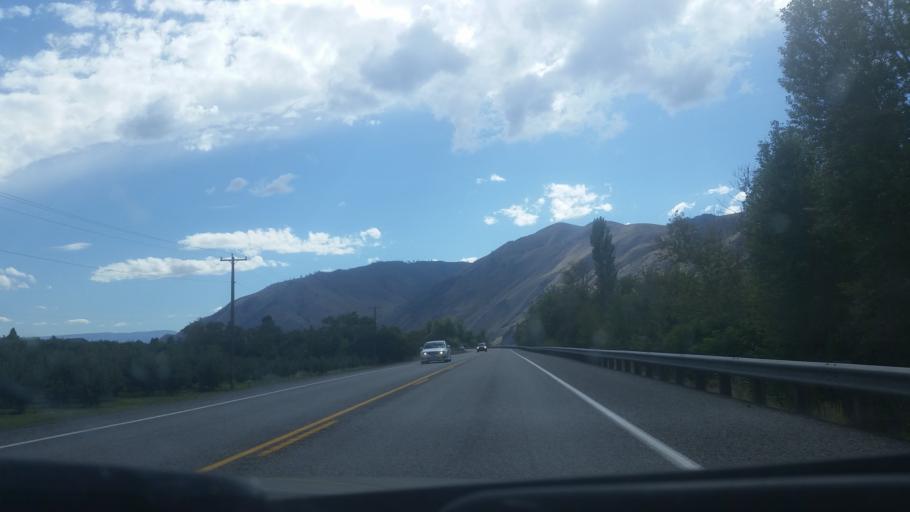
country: US
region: Washington
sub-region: Chelan County
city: Entiat
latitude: 47.6615
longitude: -120.2099
